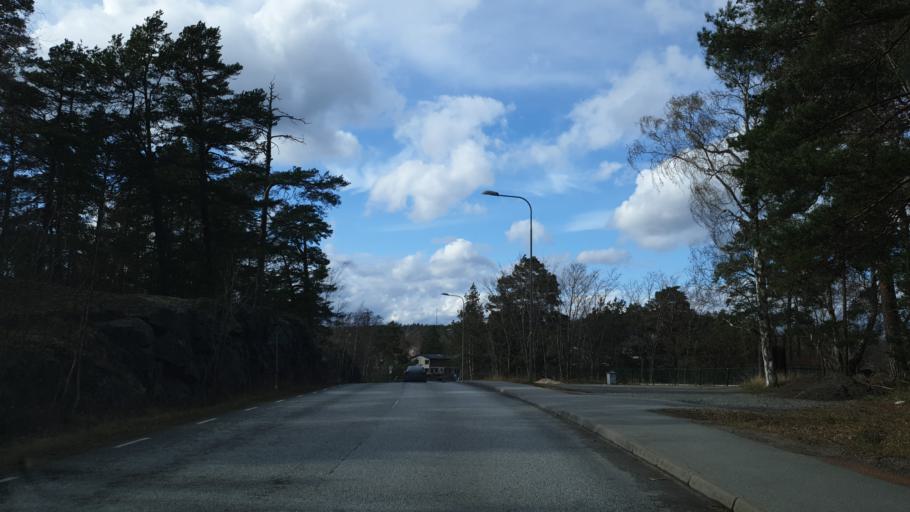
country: SE
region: Stockholm
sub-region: Nacka Kommun
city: Saltsjobaden
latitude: 59.2640
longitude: 18.3130
